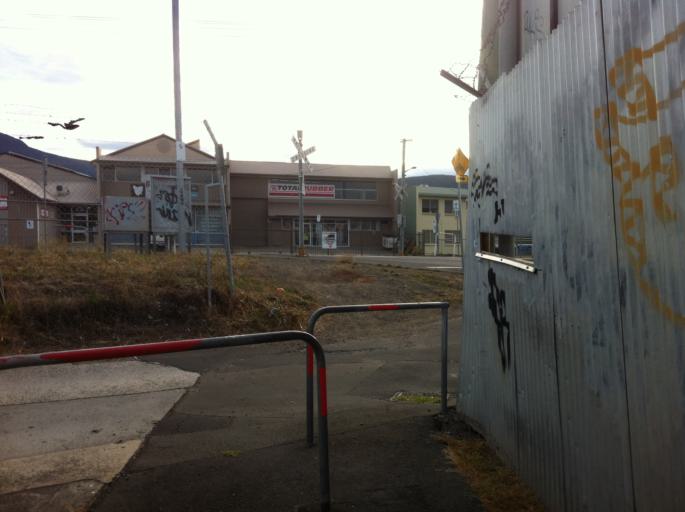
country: AU
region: Tasmania
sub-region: Glenorchy
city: Moonah
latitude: -42.8429
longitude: 147.2953
